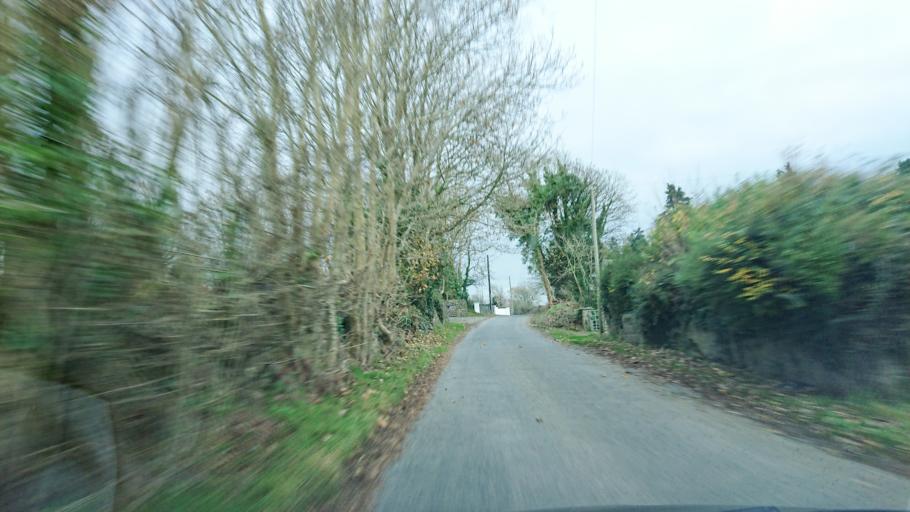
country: IE
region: Munster
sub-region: Waterford
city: Waterford
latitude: 52.2527
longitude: -7.0117
